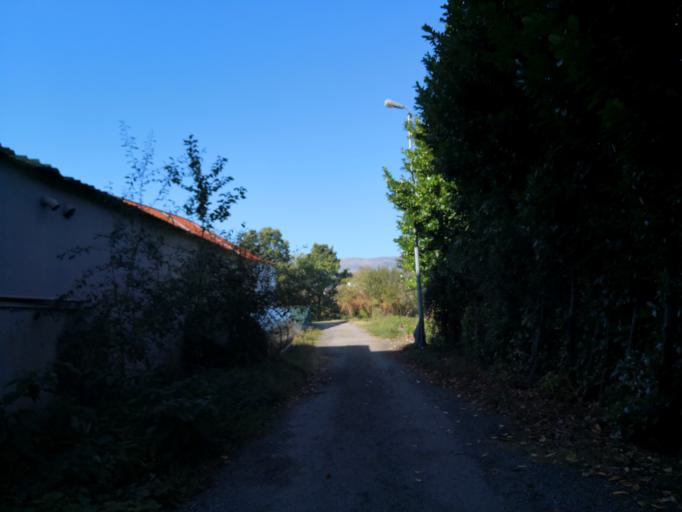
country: PT
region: Vila Real
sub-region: Vila Real
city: Vila Real
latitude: 41.3002
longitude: -7.7263
